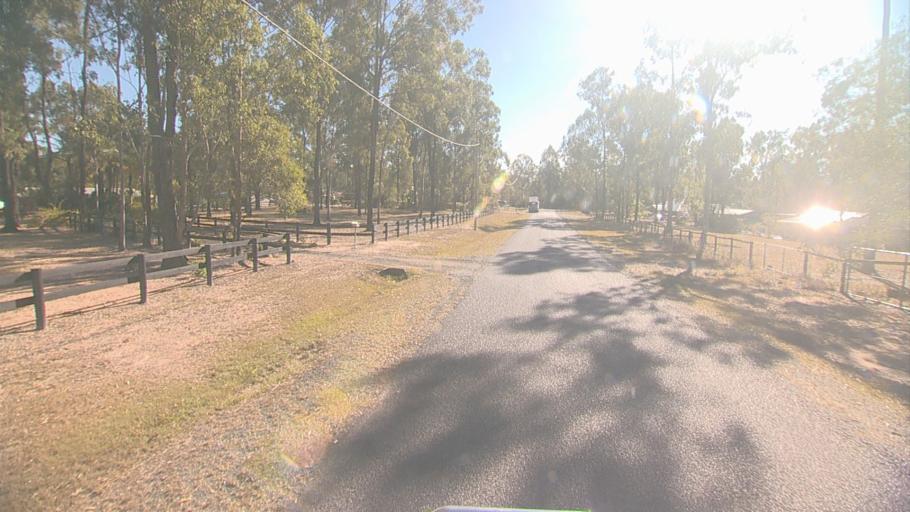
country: AU
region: Queensland
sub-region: Logan
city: North Maclean
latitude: -27.8104
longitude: 152.9710
